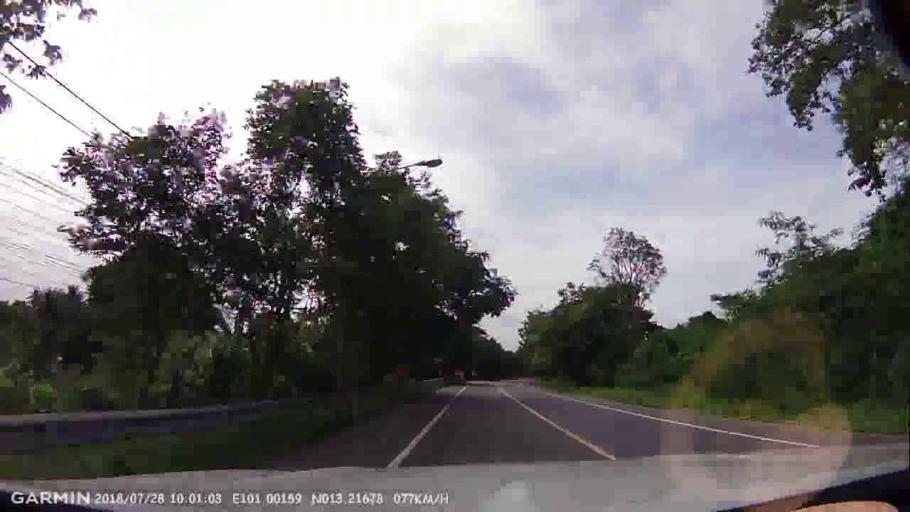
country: TH
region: Chon Buri
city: Si Racha
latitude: 13.2164
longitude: 101.0018
